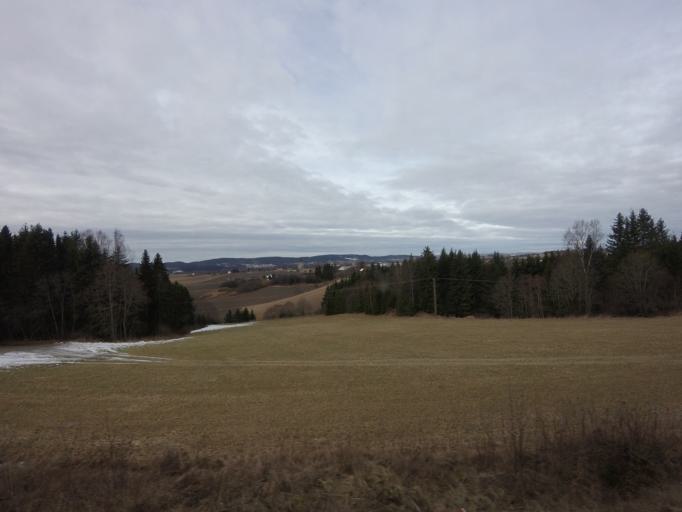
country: NO
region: Akershus
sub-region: Fet
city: Fetsund
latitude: 59.9147
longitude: 11.1841
